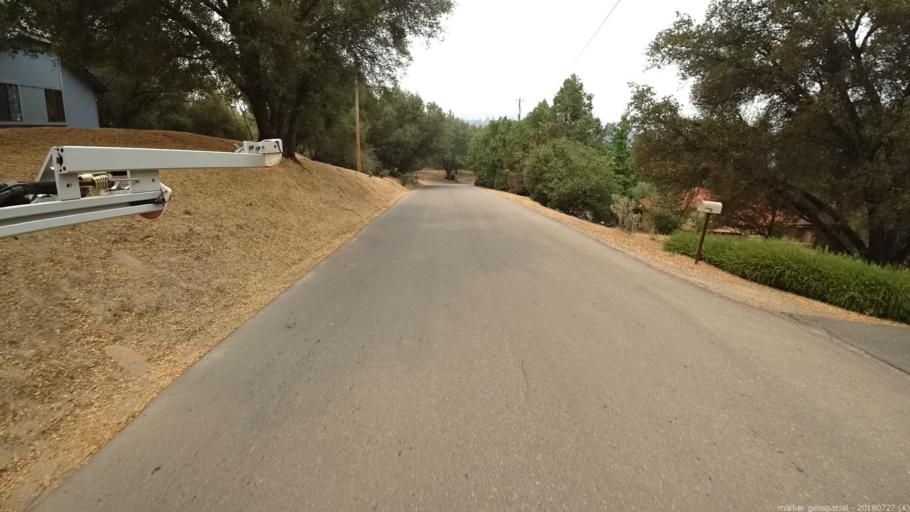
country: US
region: California
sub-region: Madera County
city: Oakhurst
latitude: 37.3310
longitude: -119.6299
